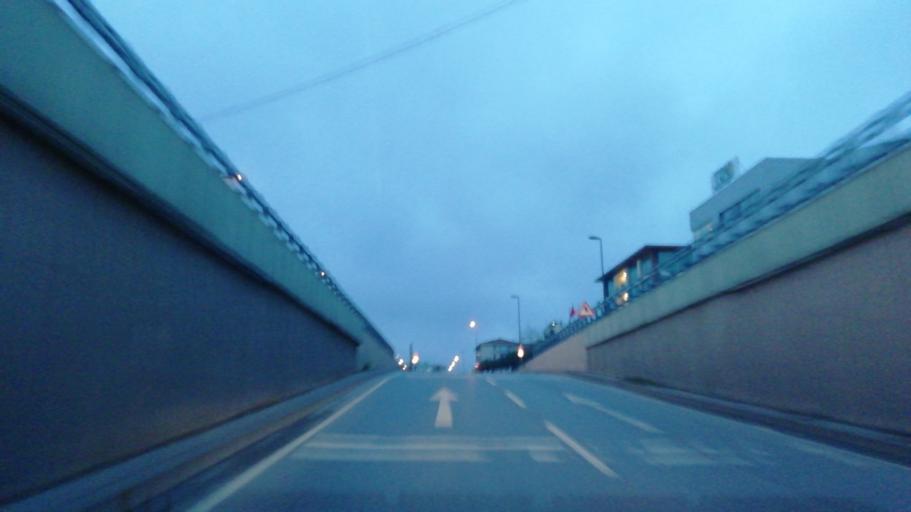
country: TR
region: Istanbul
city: Mahmutbey
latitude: 41.0120
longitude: 28.8180
